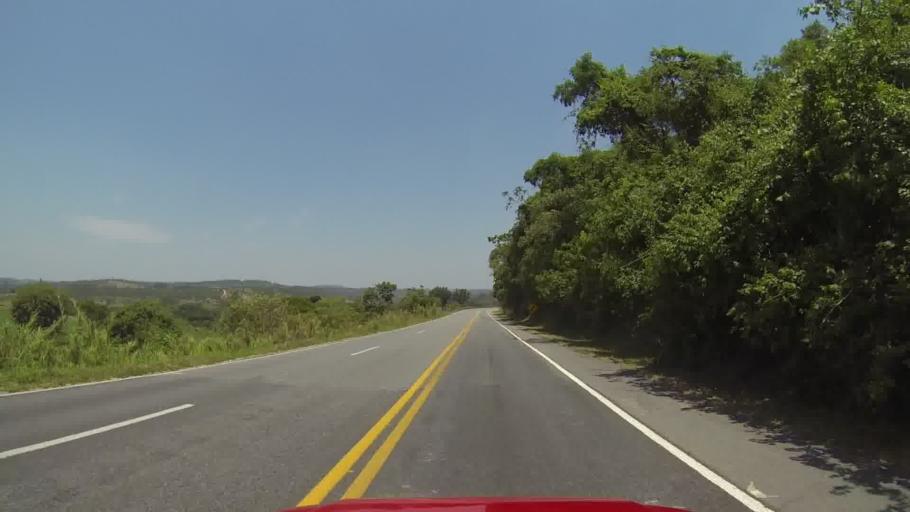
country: BR
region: Minas Gerais
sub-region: Itapecerica
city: Itapecerica
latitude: -20.2932
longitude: -45.1587
